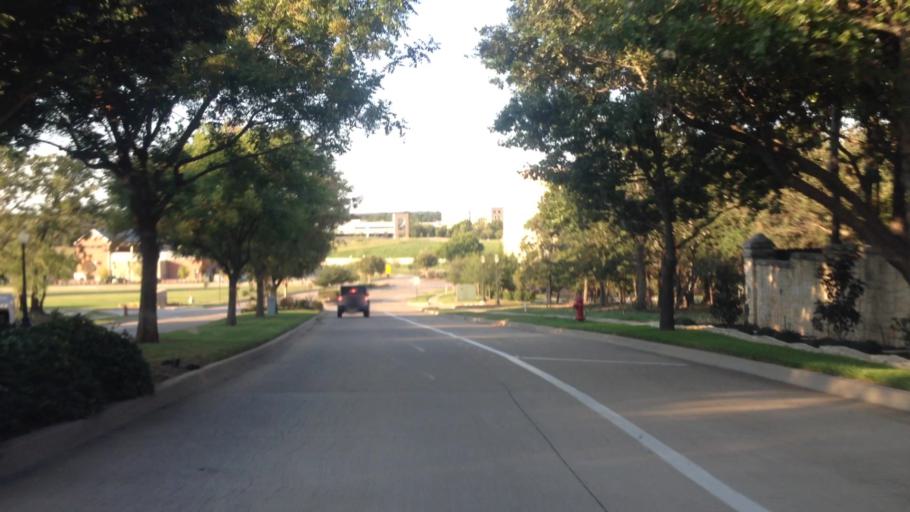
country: US
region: Texas
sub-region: Denton County
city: Trophy Club
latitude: 32.9885
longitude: -97.1697
